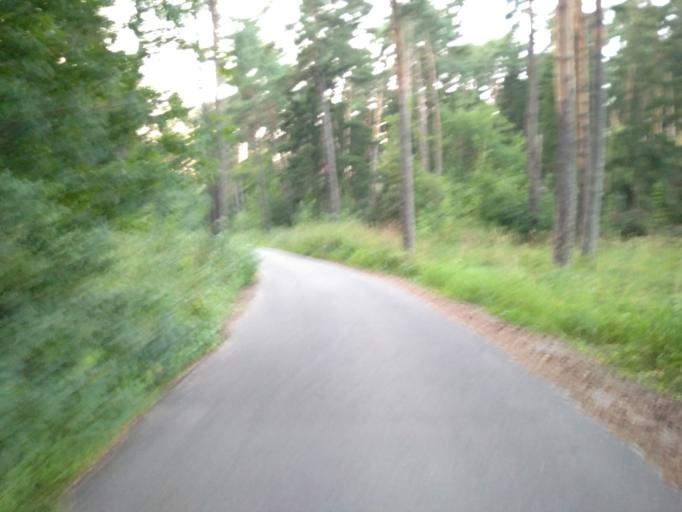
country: RU
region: Moskovskaya
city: Zhukovskiy
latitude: 55.5787
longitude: 38.1168
